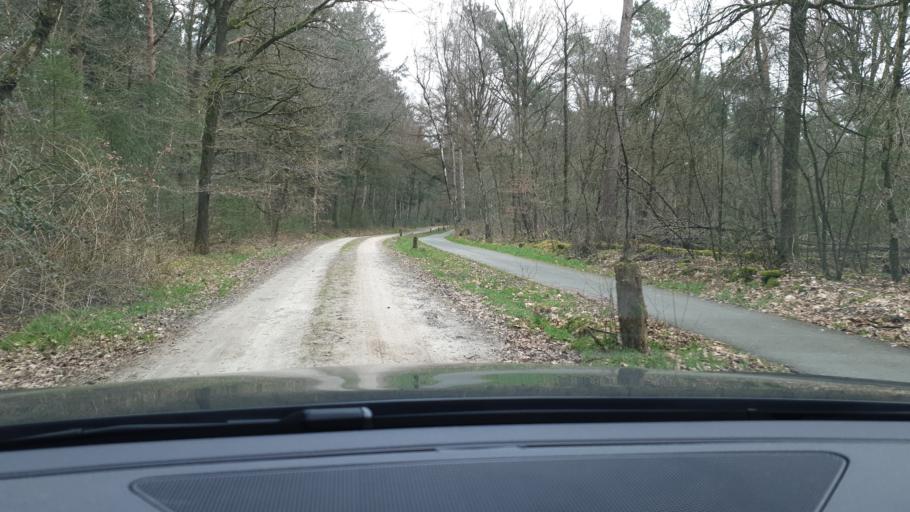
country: NL
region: North Brabant
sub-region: Gemeente Veldhoven
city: Oerle
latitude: 51.4198
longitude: 5.3288
